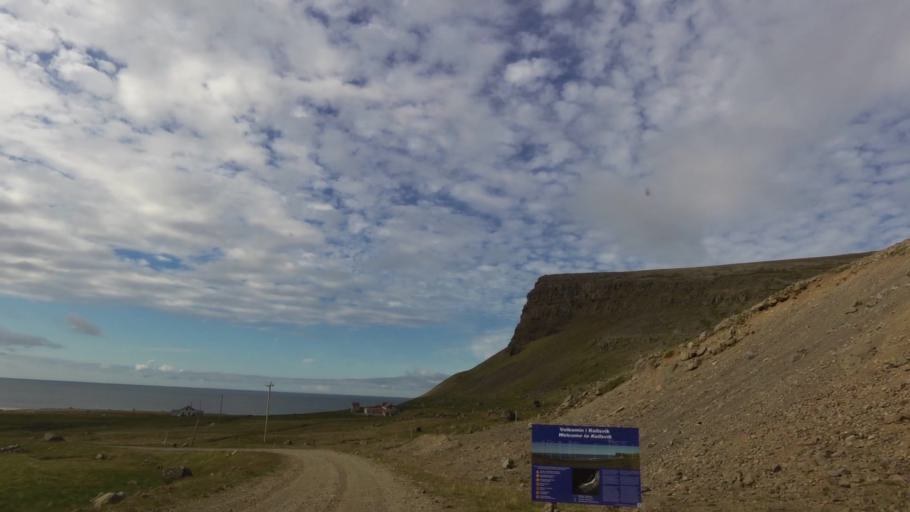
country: IS
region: West
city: Olafsvik
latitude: 65.6136
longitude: -24.3138
